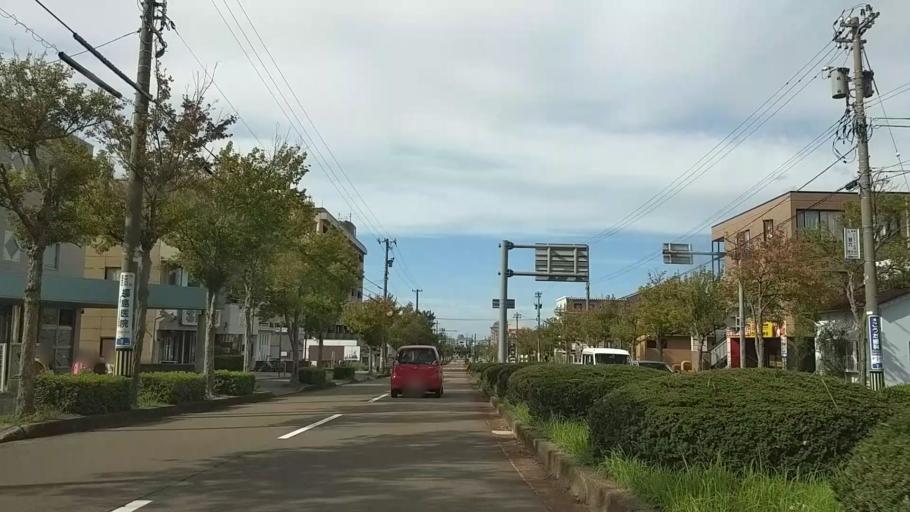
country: JP
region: Ishikawa
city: Nonoichi
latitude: 36.5246
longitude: 136.6391
